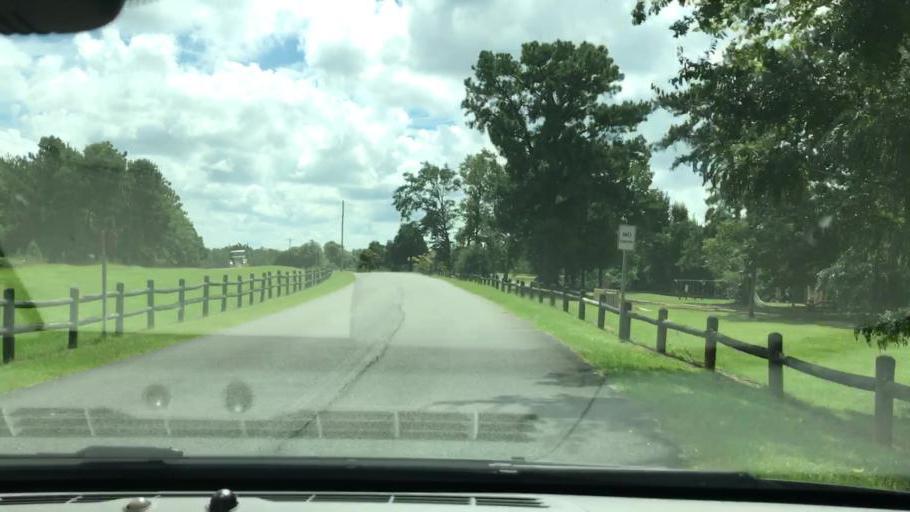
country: US
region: Georgia
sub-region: Stewart County
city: Lumpkin
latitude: 32.0693
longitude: -84.9069
